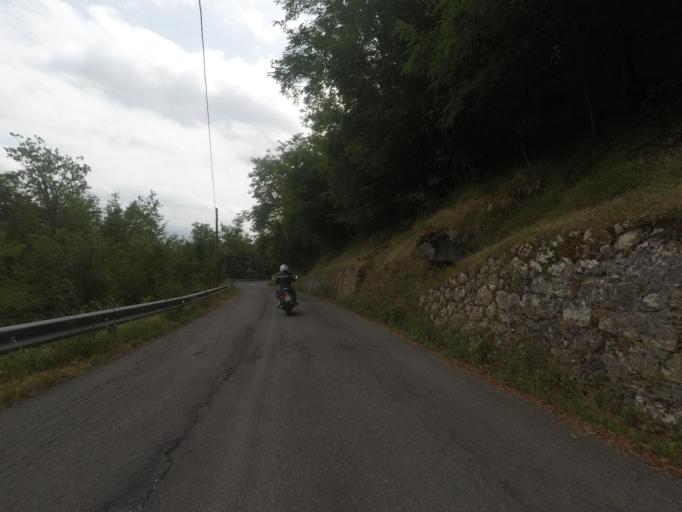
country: IT
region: Tuscany
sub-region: Provincia di Lucca
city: Castelnuovo di Garfagnana
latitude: 44.1107
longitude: 10.3697
